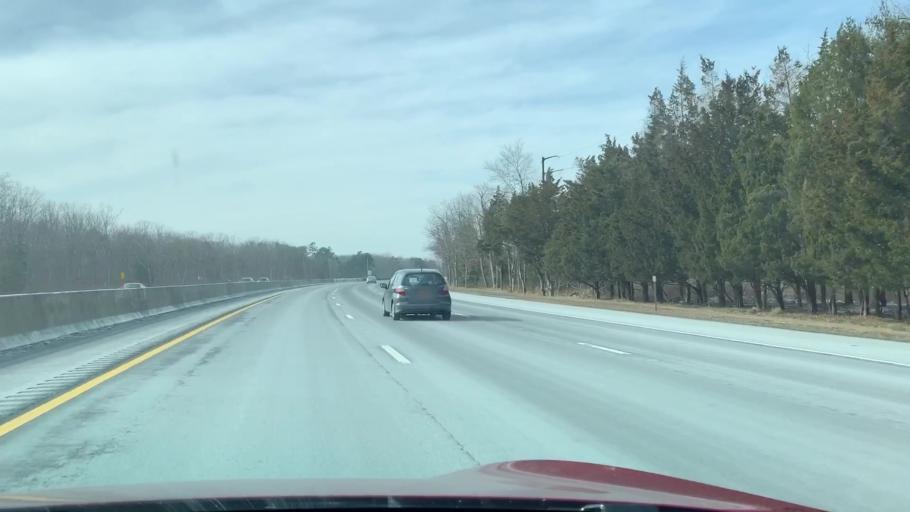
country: US
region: New Jersey
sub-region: Atlantic County
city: Port Republic
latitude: 39.5425
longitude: -74.4724
